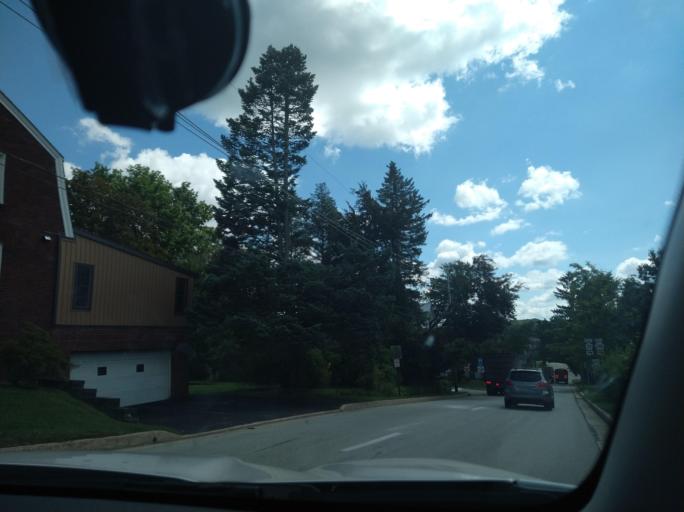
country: US
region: Pennsylvania
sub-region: Somerset County
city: Somerset
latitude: 40.0084
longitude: -79.0921
